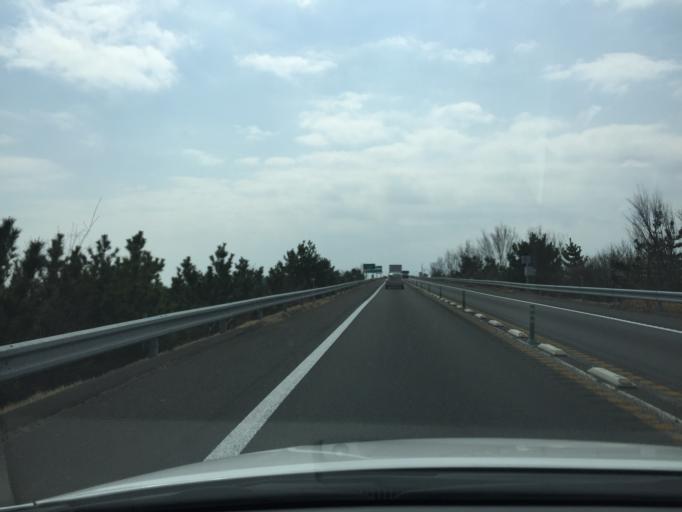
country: JP
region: Miyagi
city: Iwanuma
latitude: 38.0996
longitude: 140.8889
